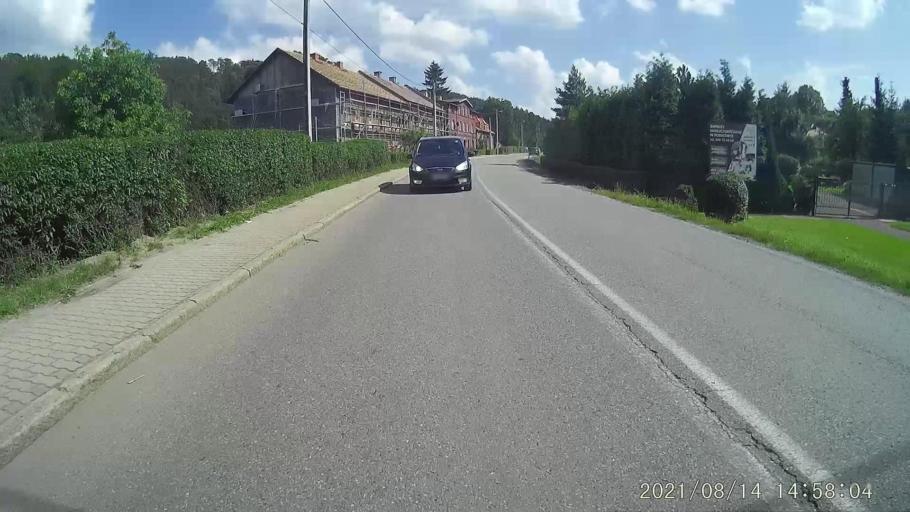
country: PL
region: Lower Silesian Voivodeship
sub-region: Powiat walbrzyski
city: Gluszyca
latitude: 50.7016
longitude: 16.3651
